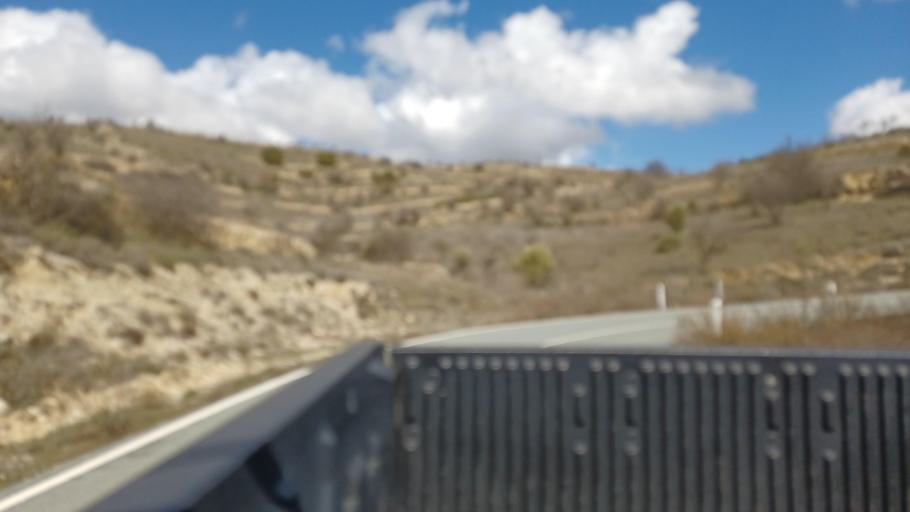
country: CY
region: Limassol
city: Pachna
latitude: 34.8122
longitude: 32.7600
